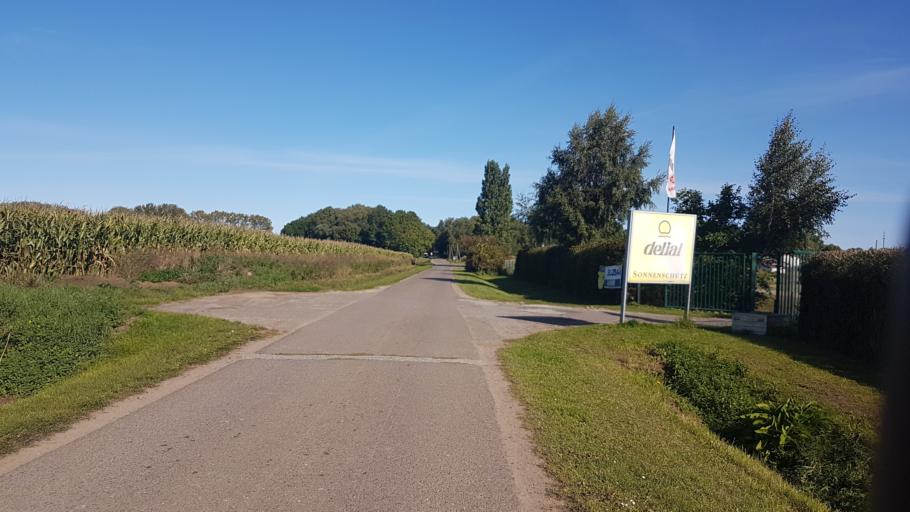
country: DE
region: Mecklenburg-Vorpommern
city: Sagard
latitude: 54.5162
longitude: 13.5304
